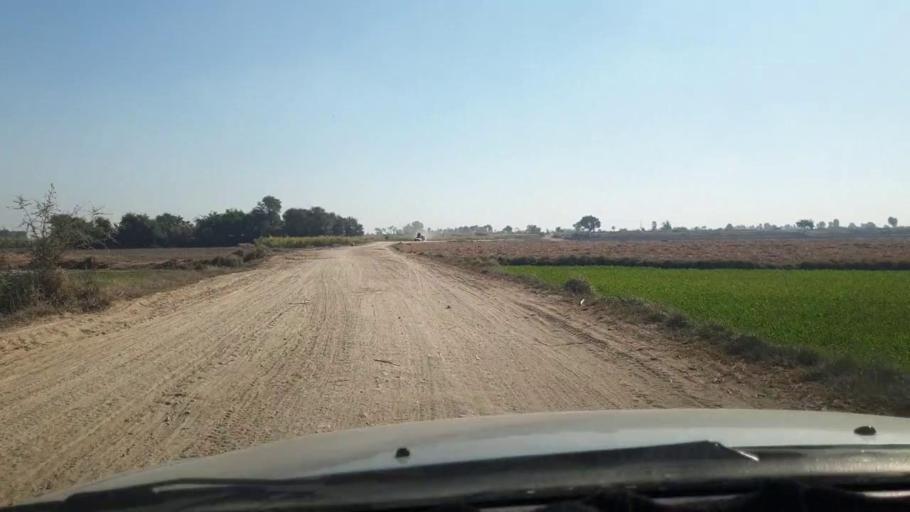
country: PK
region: Sindh
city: Ghotki
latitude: 28.0193
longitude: 69.2233
